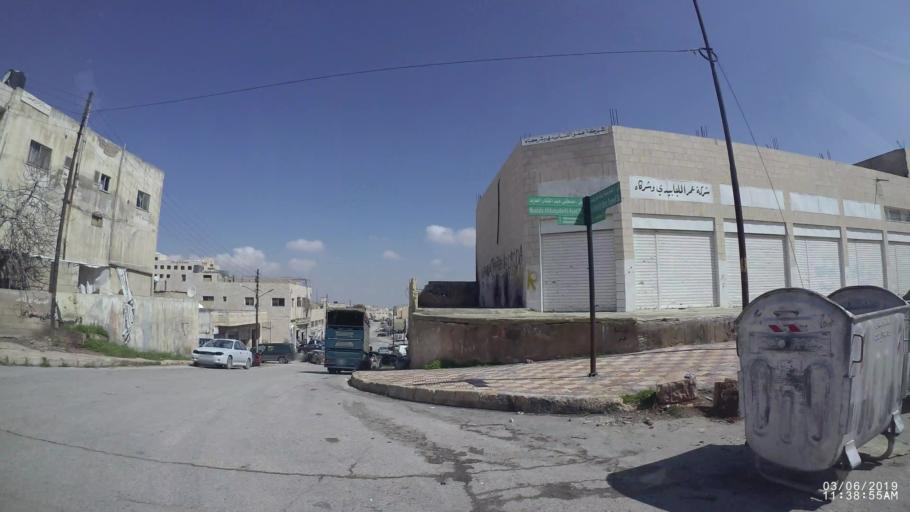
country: JO
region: Zarqa
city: Russeifa
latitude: 31.9824
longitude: 35.9993
